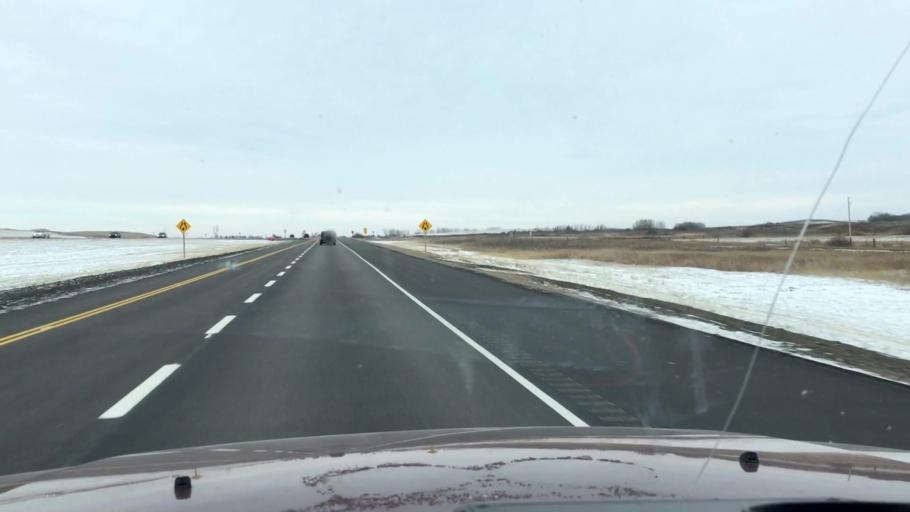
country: CA
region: Saskatchewan
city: Moose Jaw
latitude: 50.8645
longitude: -105.5951
